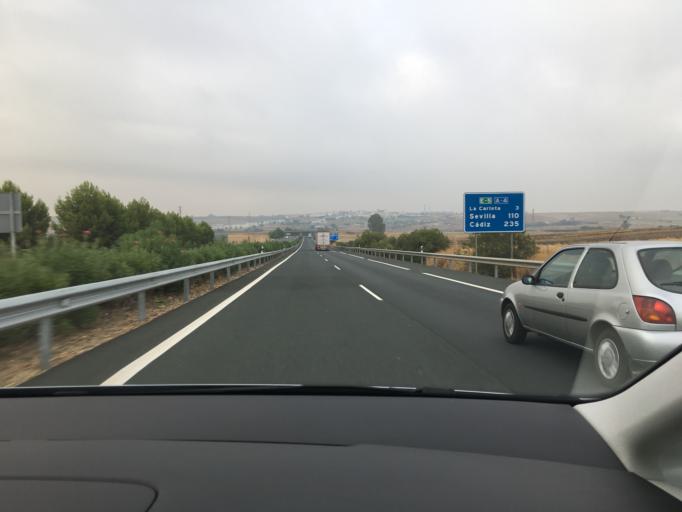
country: ES
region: Andalusia
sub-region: Province of Cordoba
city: La Carlota
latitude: 37.6912
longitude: -4.9215
